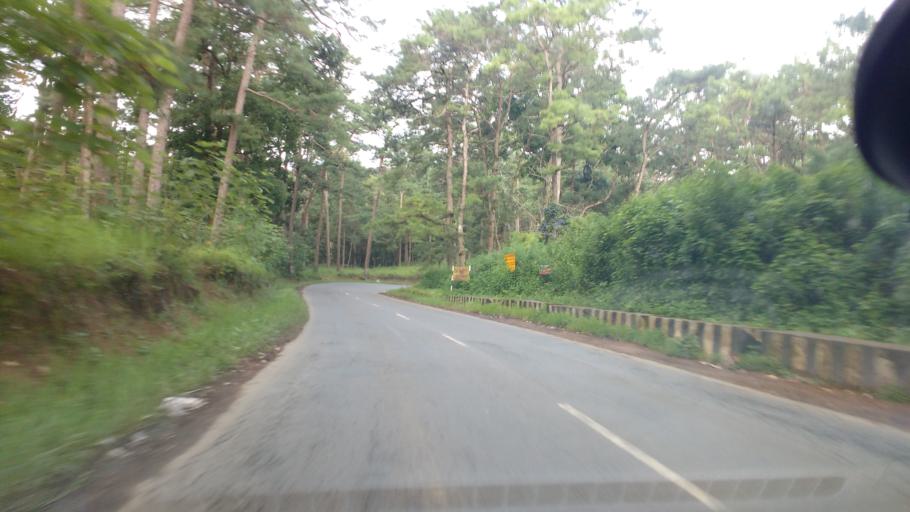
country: IN
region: Meghalaya
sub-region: East Khasi Hills
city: Shillong
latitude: 25.5659
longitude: 91.8595
